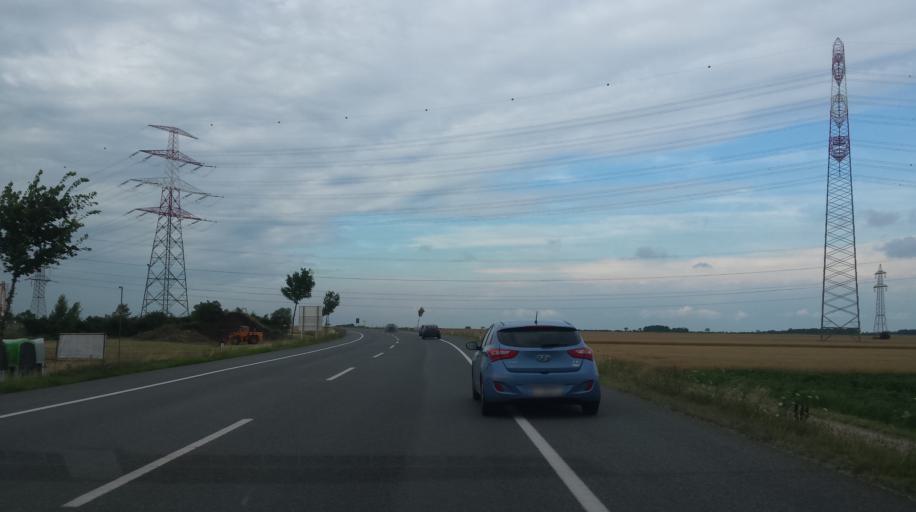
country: AT
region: Lower Austria
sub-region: Politischer Bezirk Wien-Umgebung
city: Himberg
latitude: 48.0728
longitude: 16.4601
